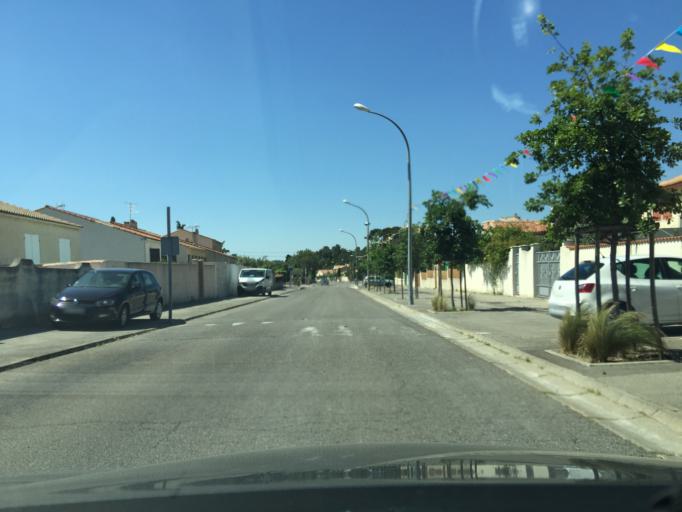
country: FR
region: Provence-Alpes-Cote d'Azur
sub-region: Departement des Bouches-du-Rhone
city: La Penne-sur-Huveaune
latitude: 43.2784
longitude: 5.5091
